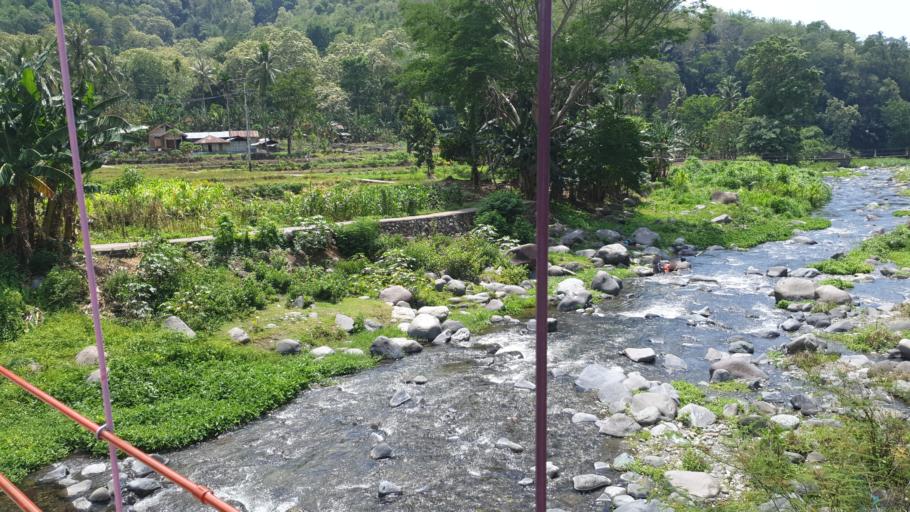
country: ID
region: East Nusa Tenggara
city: Aemura
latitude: -8.8018
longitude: 121.6710
